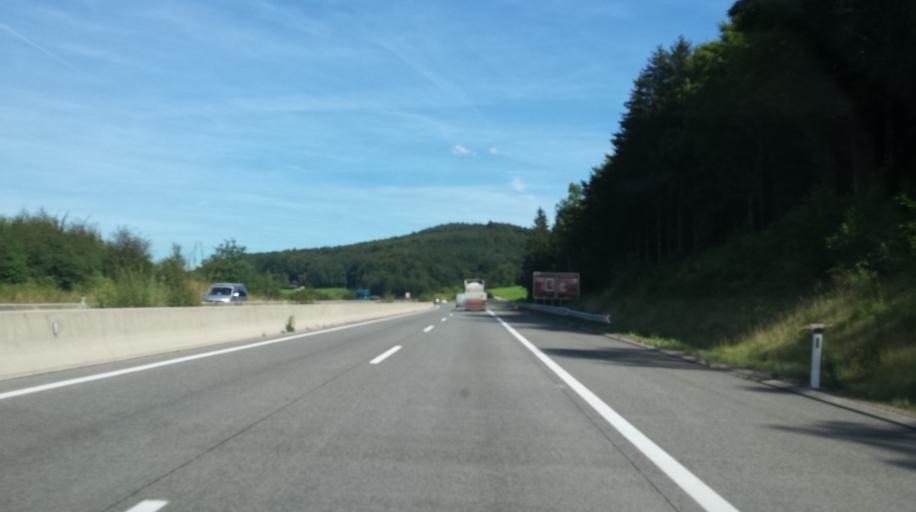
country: AT
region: Upper Austria
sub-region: Politischer Bezirk Vocklabruck
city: Aurach am Hongar
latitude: 47.9507
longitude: 13.7032
